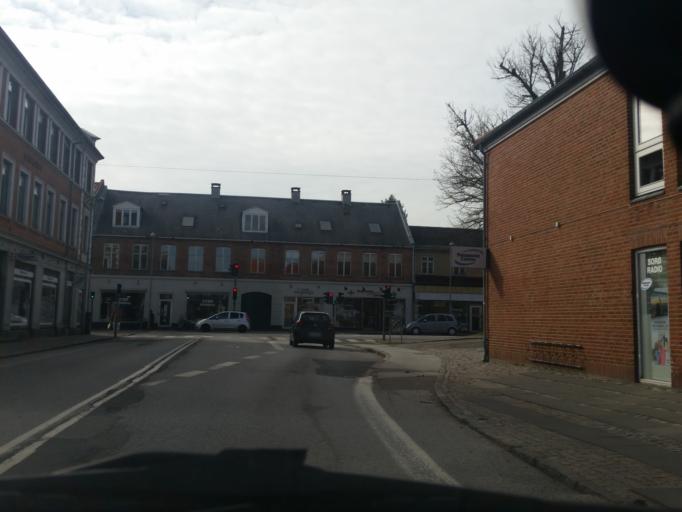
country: DK
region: Zealand
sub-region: Soro Kommune
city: Soro
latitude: 55.4346
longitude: 11.5584
